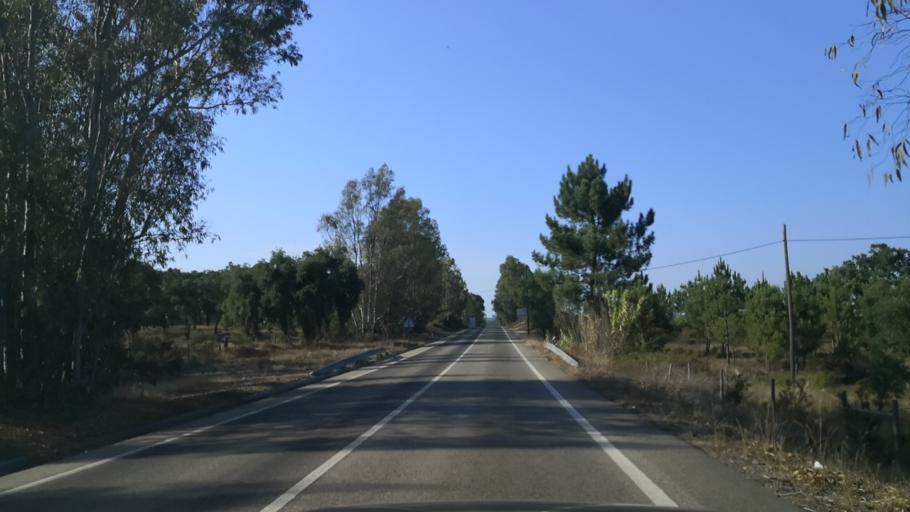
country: PT
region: Santarem
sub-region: Almeirim
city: Fazendas de Almeirim
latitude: 39.0780
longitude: -8.5670
